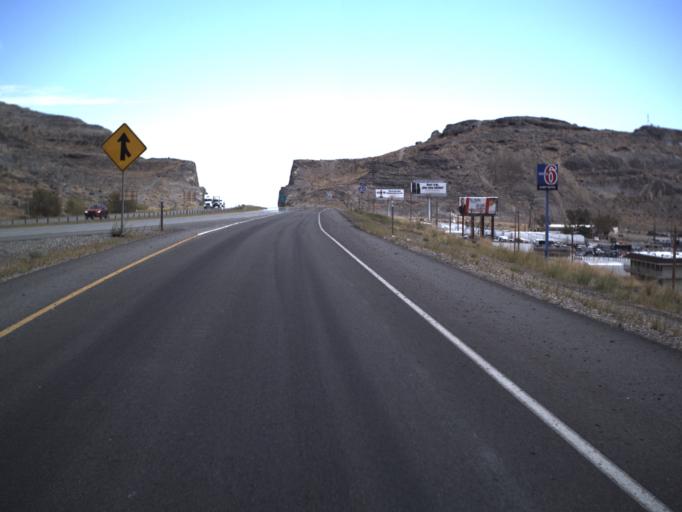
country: US
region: Utah
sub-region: Tooele County
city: Wendover
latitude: 40.7384
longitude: -114.0401
